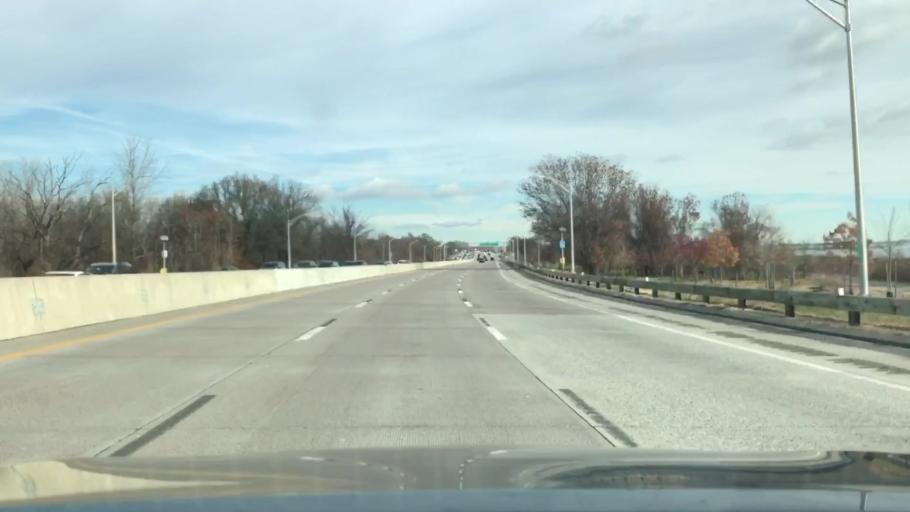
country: US
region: New York
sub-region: Kings County
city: East New York
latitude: 40.6255
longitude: -73.8935
